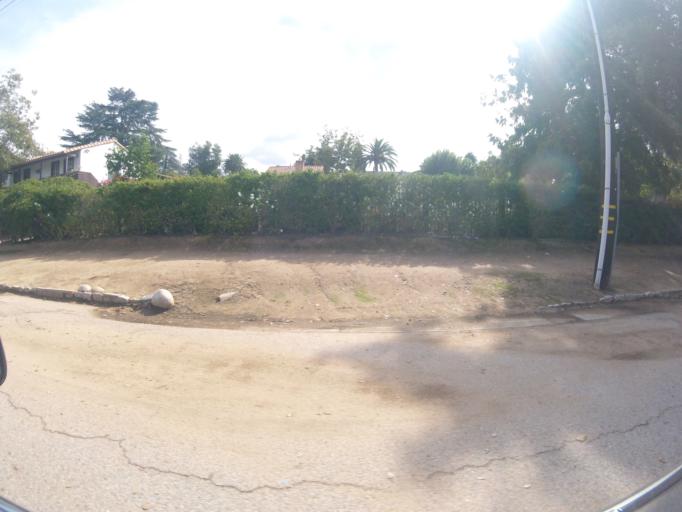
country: US
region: California
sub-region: San Bernardino County
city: Redlands
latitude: 34.0388
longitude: -117.1789
